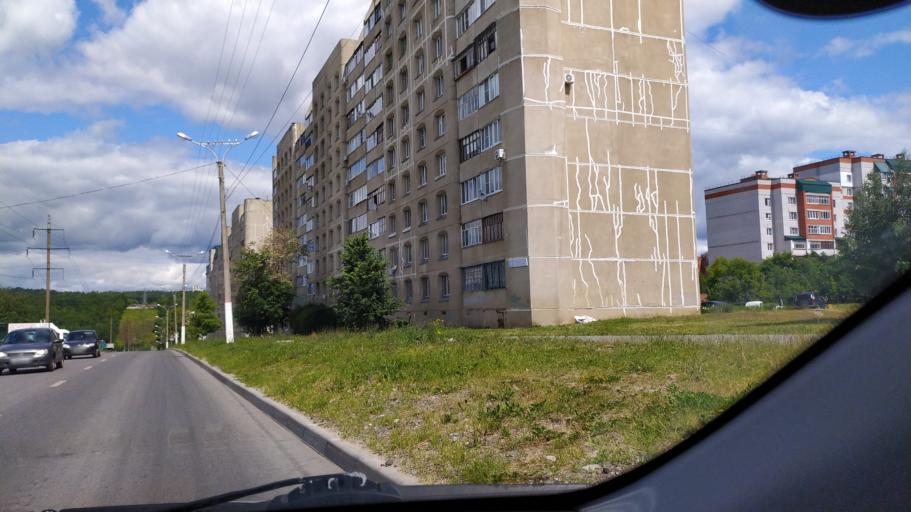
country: RU
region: Chuvashia
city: Novyye Lapsary
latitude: 56.1178
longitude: 47.1753
